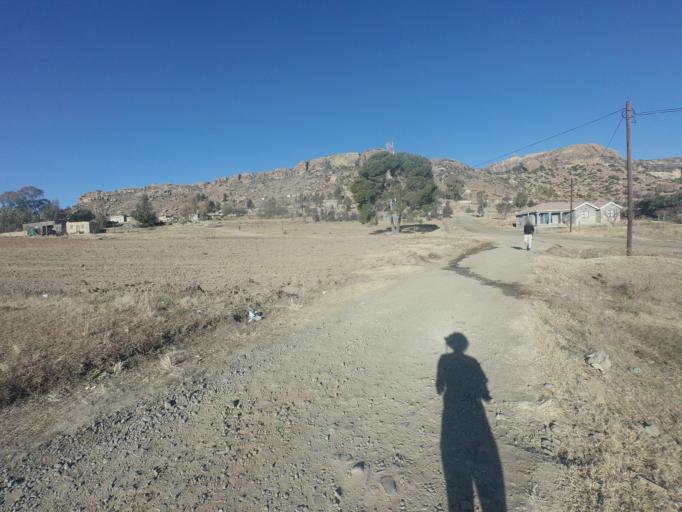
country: LS
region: Maseru
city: Maseru
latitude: -29.3024
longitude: 27.5488
